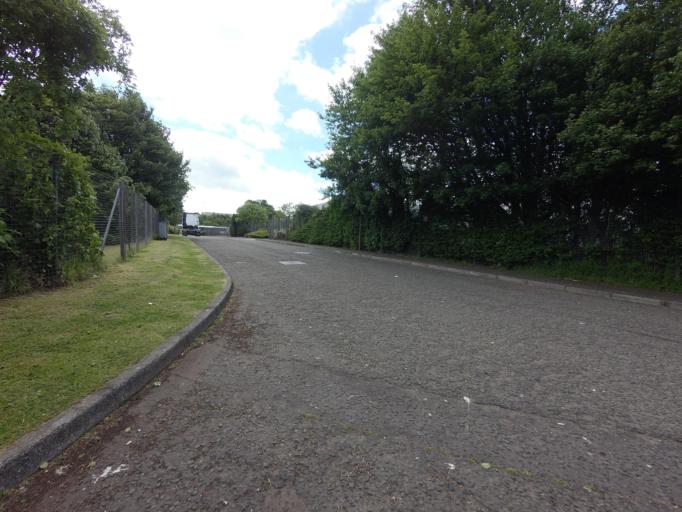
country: GB
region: Scotland
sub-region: West Lothian
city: Livingston
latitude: 55.9156
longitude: -3.5146
